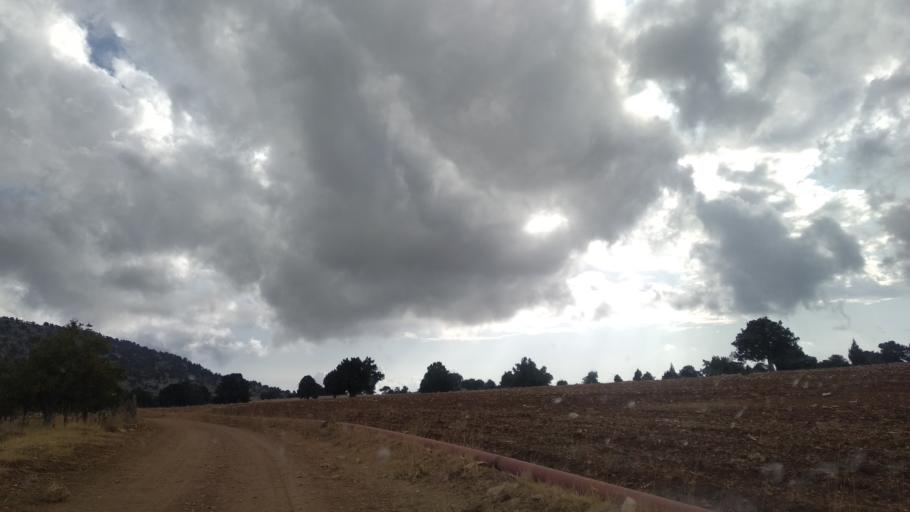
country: TR
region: Mersin
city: Sarikavak
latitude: 36.5641
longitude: 33.7374
